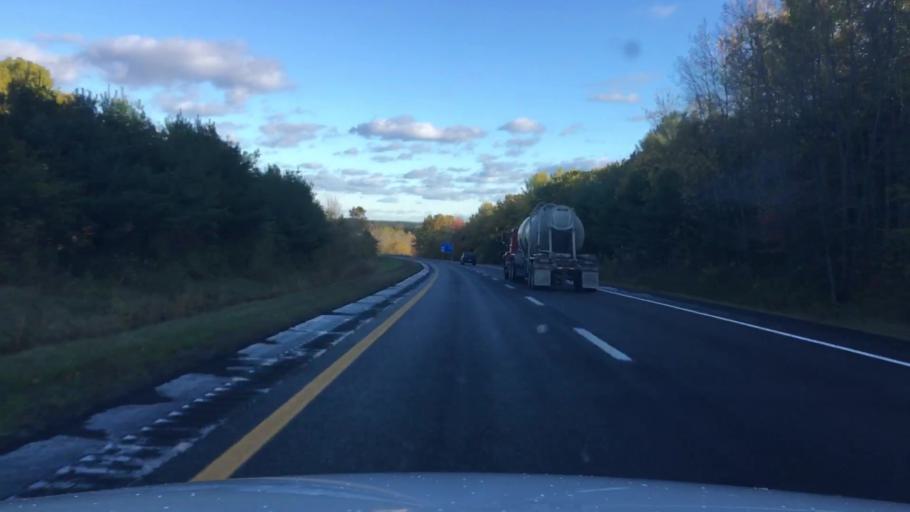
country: US
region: Maine
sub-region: Penobscot County
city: Orono
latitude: 44.8948
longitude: -68.6910
